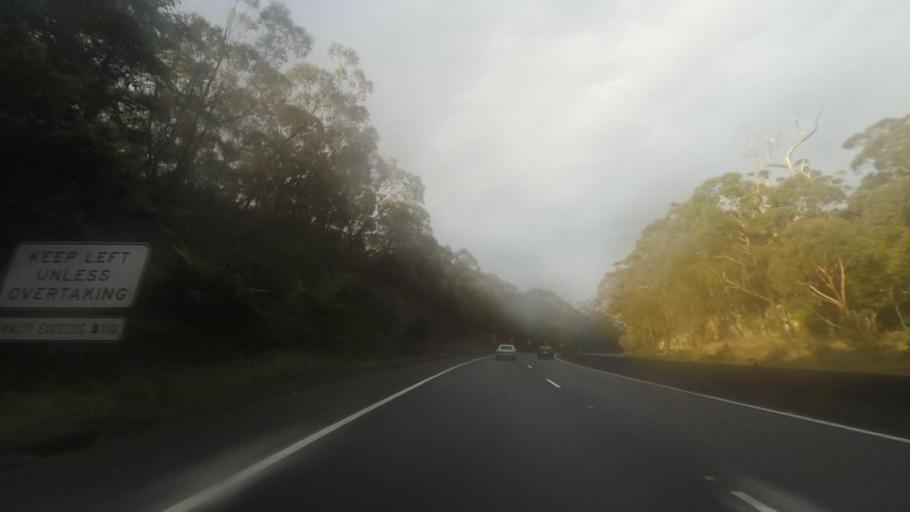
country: AU
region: New South Wales
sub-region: Wollongong
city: Bulli
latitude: -34.3464
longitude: 150.8712
